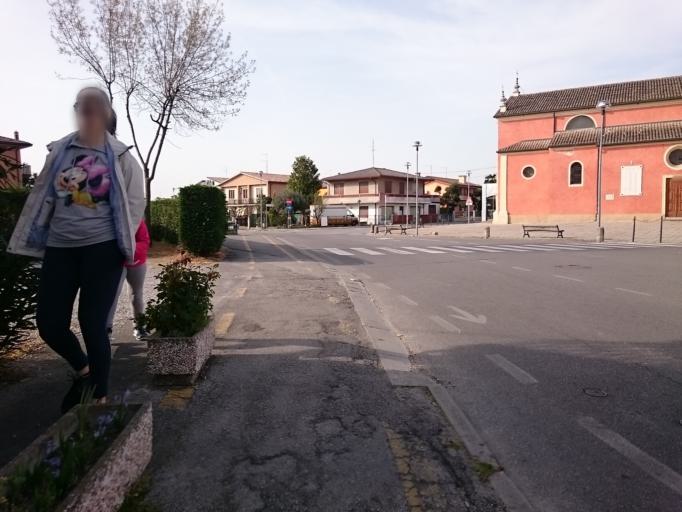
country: IT
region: Veneto
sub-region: Provincia di Padova
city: Bertipaglia
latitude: 45.3148
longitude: 11.8832
